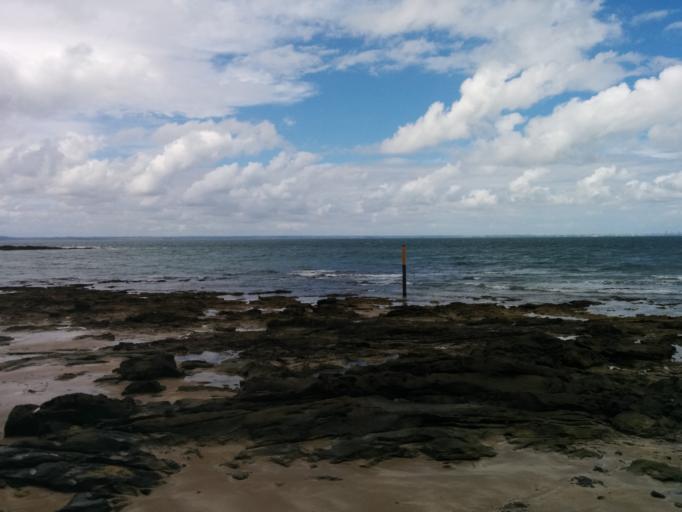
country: BR
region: Bahia
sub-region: Madre De Deus
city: Madre de Deus
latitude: -12.8149
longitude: -38.6413
